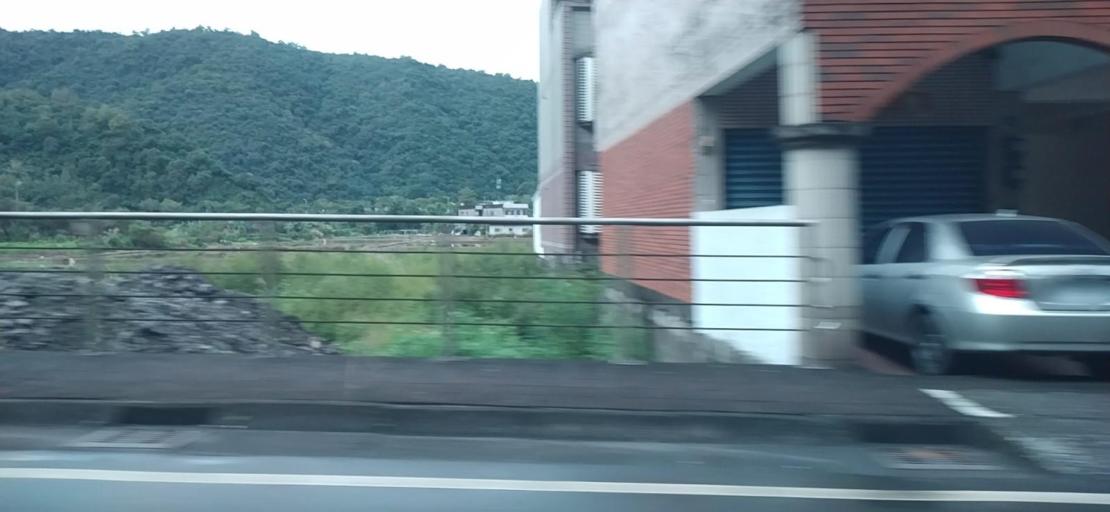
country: TW
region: Taiwan
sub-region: Yilan
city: Yilan
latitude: 24.6043
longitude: 121.8372
